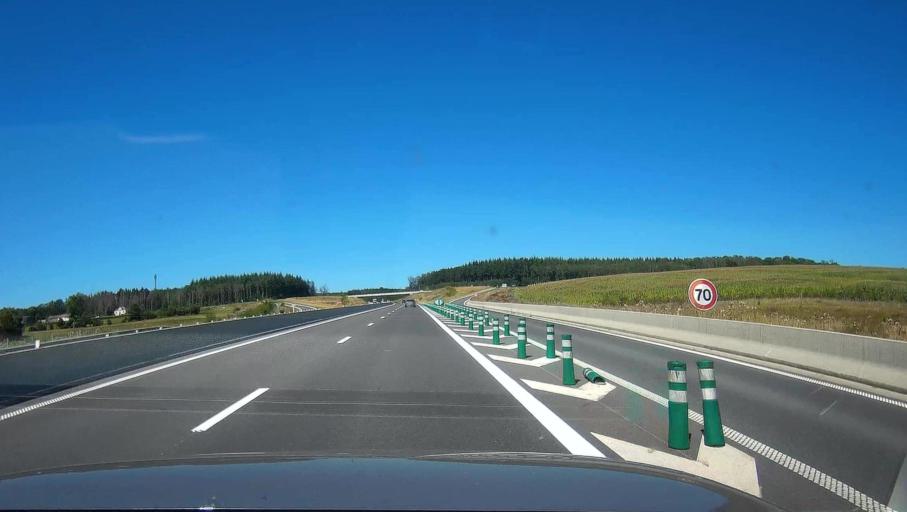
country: FR
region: Champagne-Ardenne
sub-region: Departement des Ardennes
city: Rimogne
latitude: 49.8406
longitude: 4.5131
